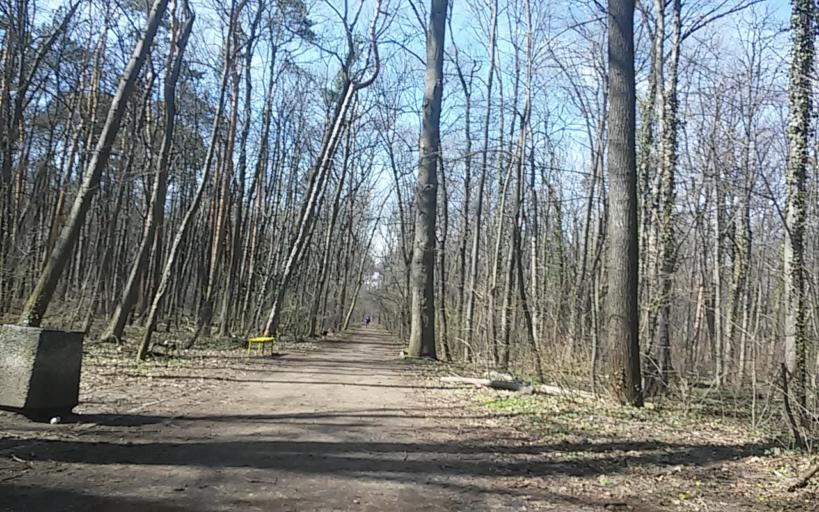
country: BG
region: Sofia-Capital
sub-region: Stolichna Obshtina
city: Sofia
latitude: 42.6800
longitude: 23.3490
